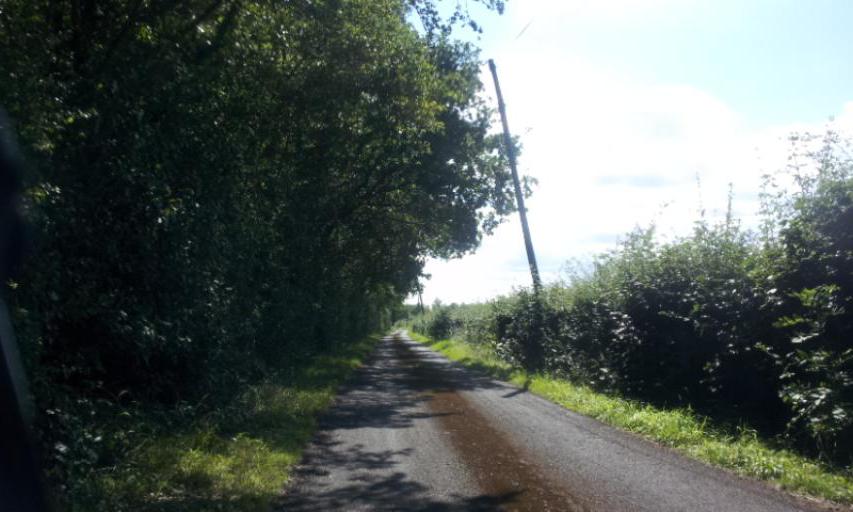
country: GB
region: England
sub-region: Kent
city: Marden
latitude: 51.1897
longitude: 0.4917
